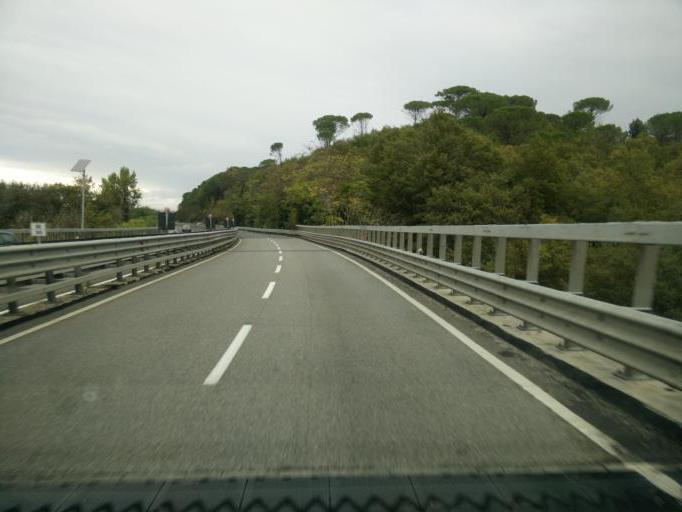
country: IT
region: Tuscany
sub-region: Province of Florence
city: Barberino Val d'Elsa
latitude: 43.5153
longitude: 11.1967
